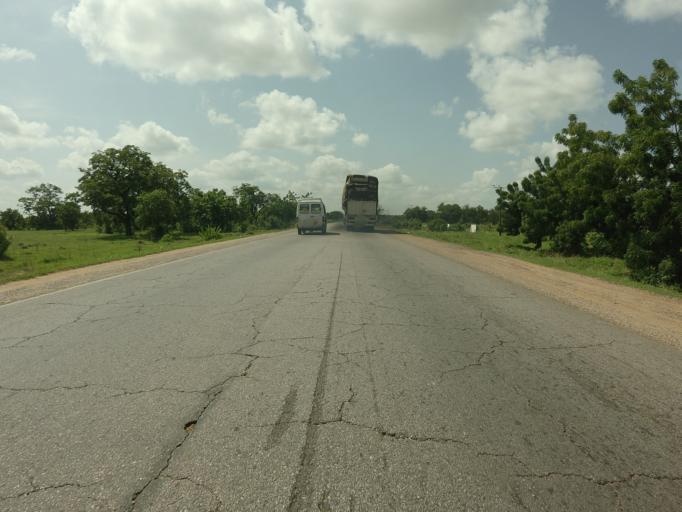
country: GH
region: Northern
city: Savelugu
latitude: 9.5624
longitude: -0.8362
